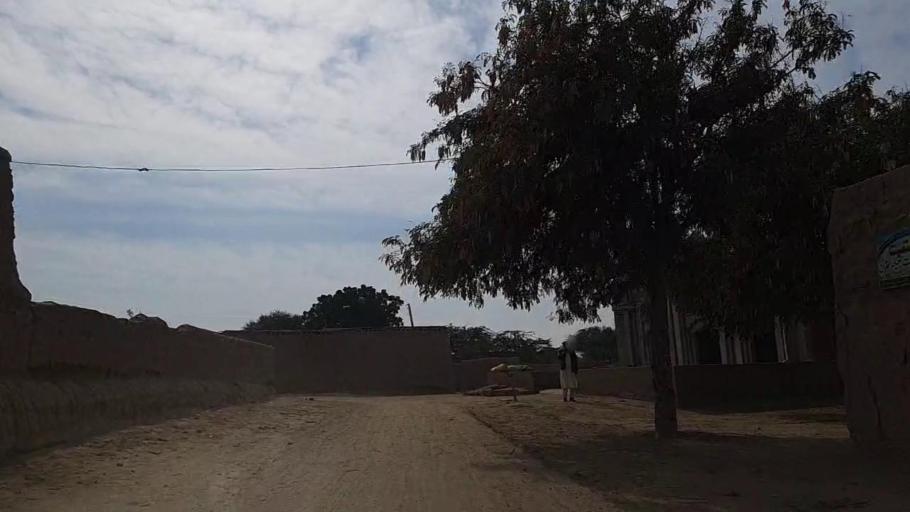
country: PK
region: Sindh
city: Nawabshah
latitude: 26.3741
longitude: 68.4450
